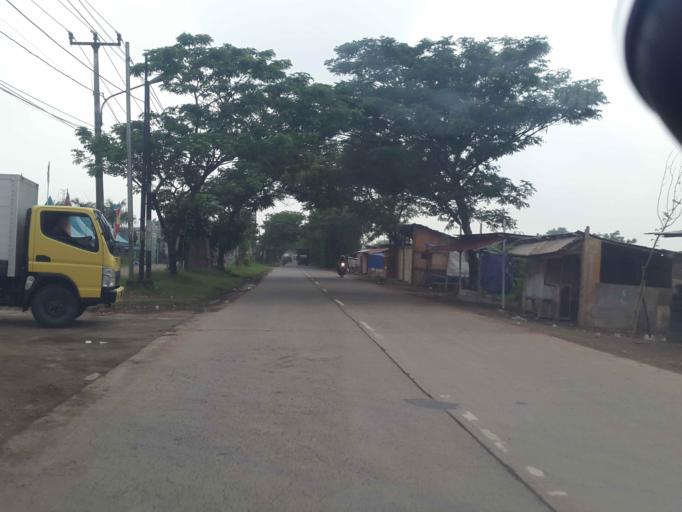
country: ID
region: West Java
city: Cikarang
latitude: -6.3175
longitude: 107.1582
